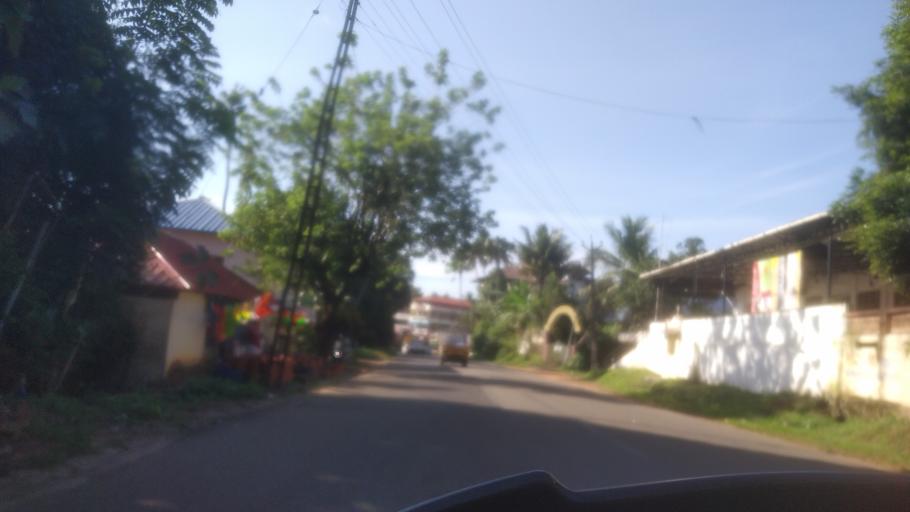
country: IN
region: Kerala
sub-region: Ernakulam
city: Ramamangalam
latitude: 9.9800
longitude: 76.5216
